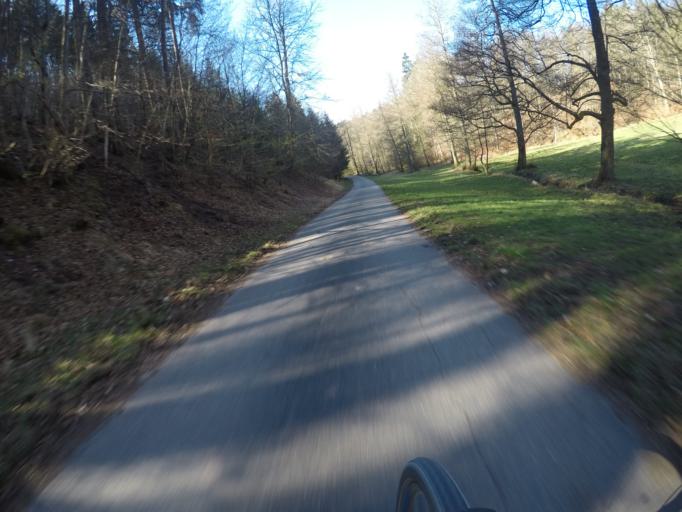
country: DE
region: Baden-Wuerttemberg
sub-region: Tuebingen Region
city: Tuebingen
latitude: 48.5621
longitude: 9.0175
